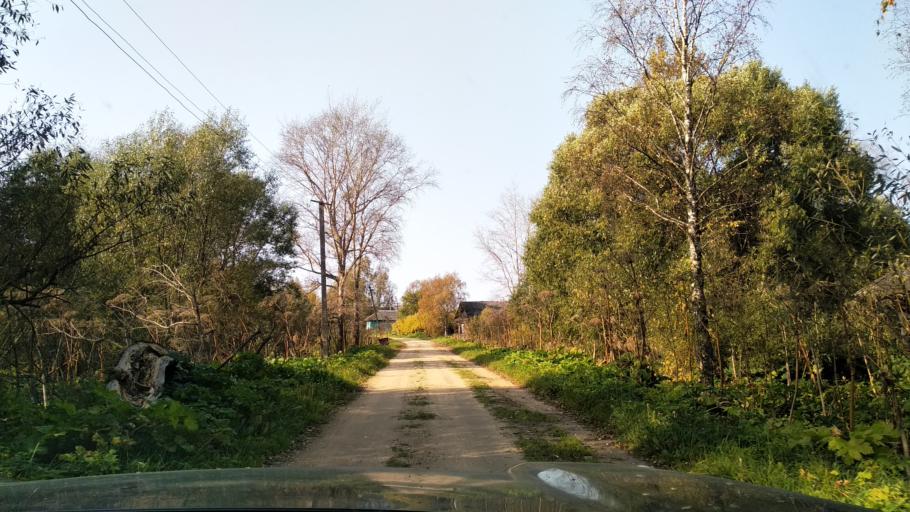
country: RU
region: Tverskaya
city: Krasnyy Kholm
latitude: 58.0336
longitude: 37.1790
